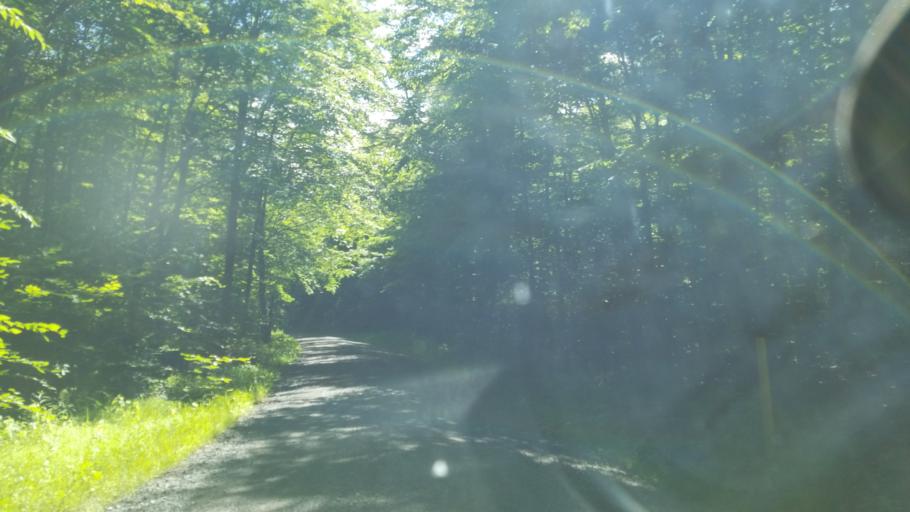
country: US
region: Pennsylvania
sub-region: Clearfield County
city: Clearfield
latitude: 41.2093
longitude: -78.4053
